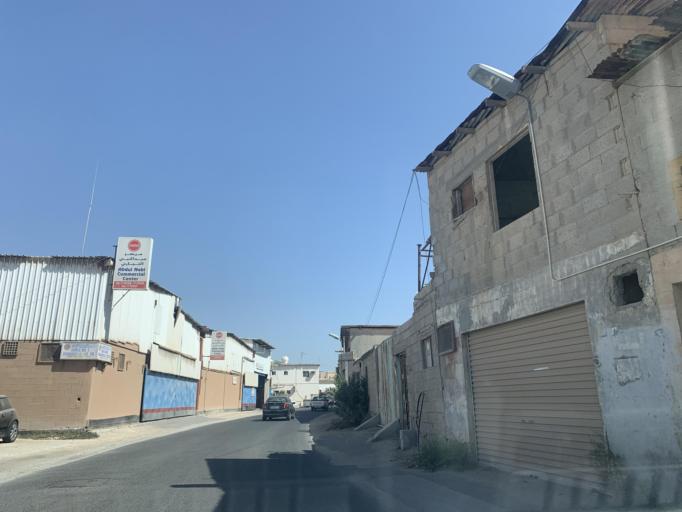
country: BH
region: Manama
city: Jidd Hafs
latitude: 26.2233
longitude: 50.5318
